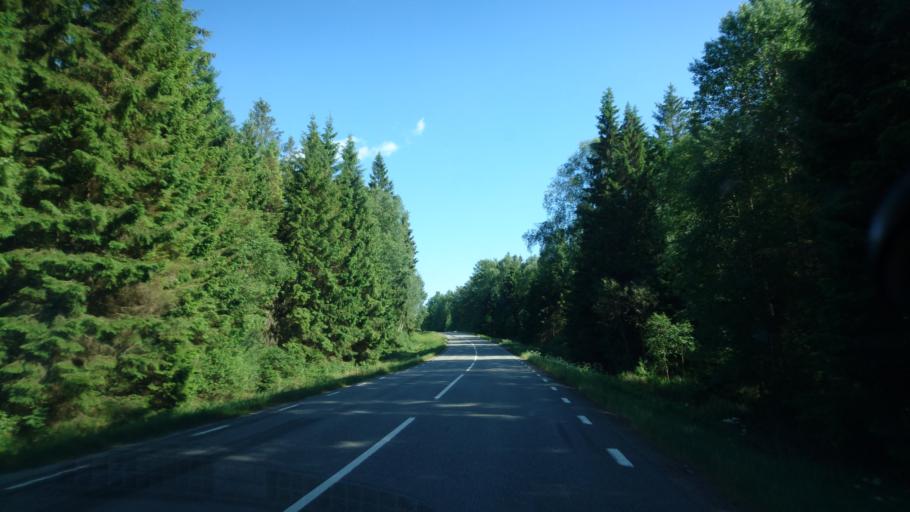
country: SE
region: Skane
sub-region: Osby Kommun
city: Lonsboda
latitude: 56.4453
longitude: 14.2380
